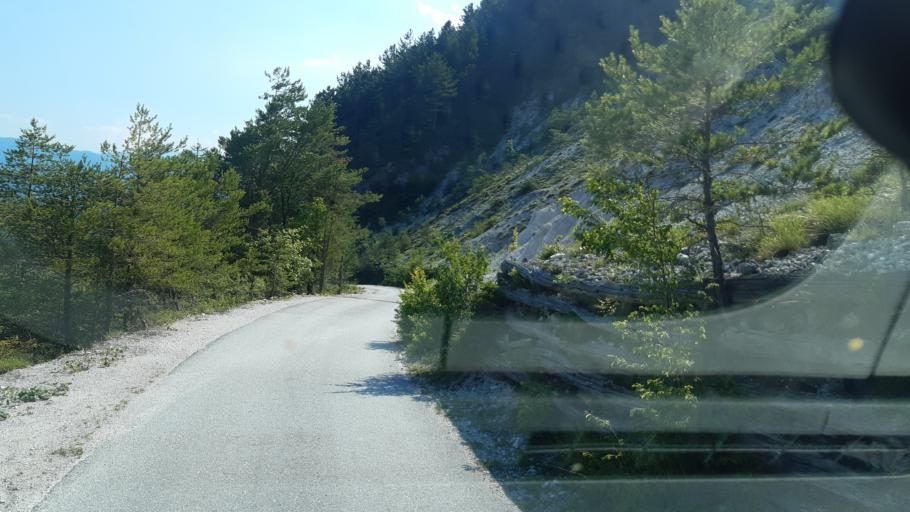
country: SI
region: Trzic
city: Bistrica pri Trzicu
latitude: 46.3635
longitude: 14.2787
